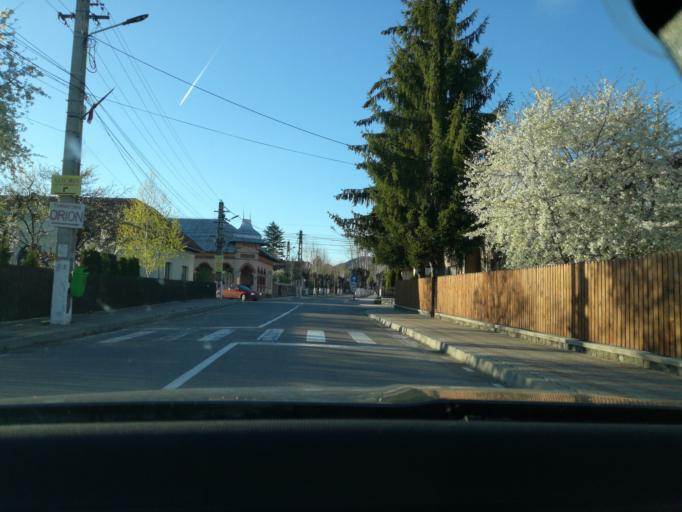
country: RO
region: Prahova
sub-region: Comuna Cornu
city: Cornu de Jos
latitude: 45.1544
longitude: 25.7037
